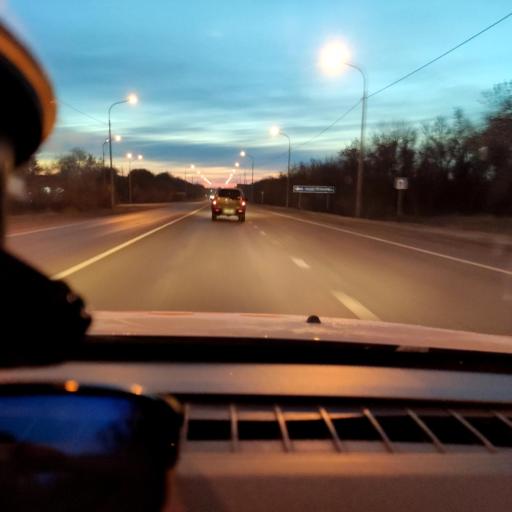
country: RU
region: Samara
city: Samara
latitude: 53.0808
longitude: 50.0903
